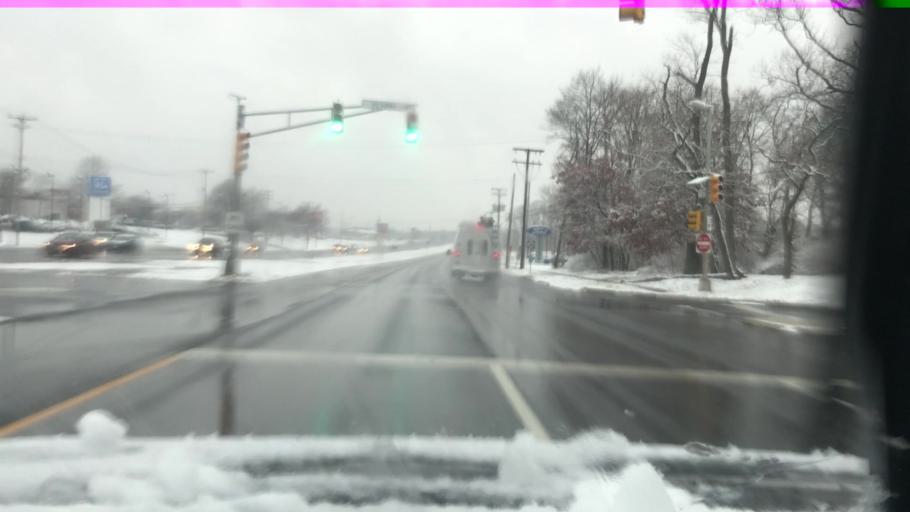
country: US
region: New Jersey
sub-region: Monmouth County
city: Eatontown
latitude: 40.2917
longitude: -74.0420
